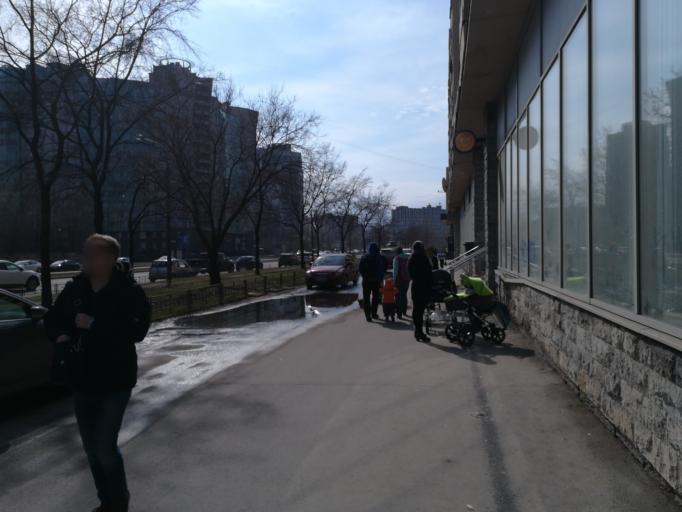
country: RU
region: St.-Petersburg
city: Vasyl'evsky Ostrov
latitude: 59.9490
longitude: 30.2431
